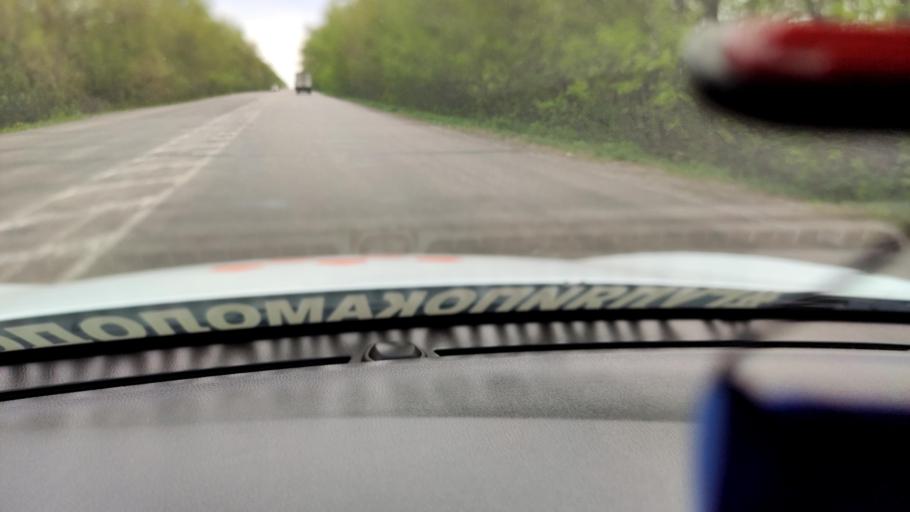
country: RU
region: Voronezj
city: Maslovka
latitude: 51.4808
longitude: 39.3069
